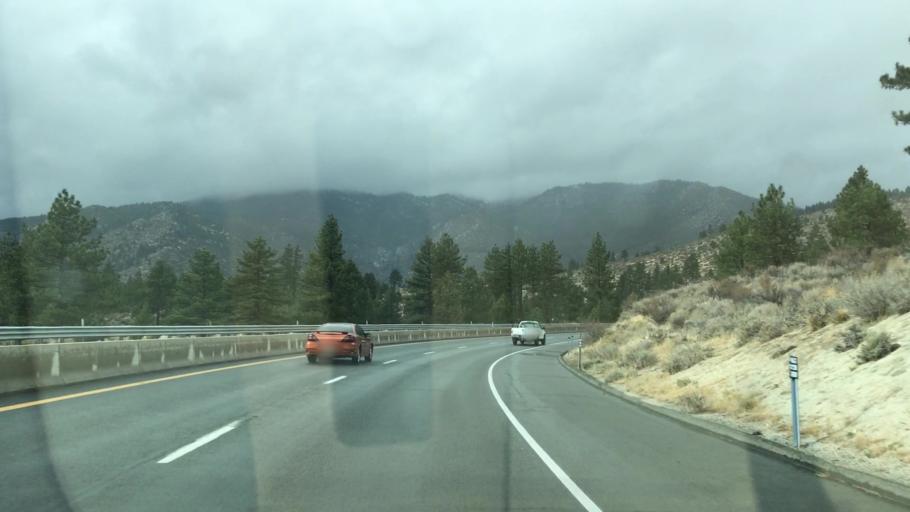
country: US
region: Nevada
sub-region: Douglas County
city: Indian Hills
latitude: 39.1182
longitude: -119.8148
